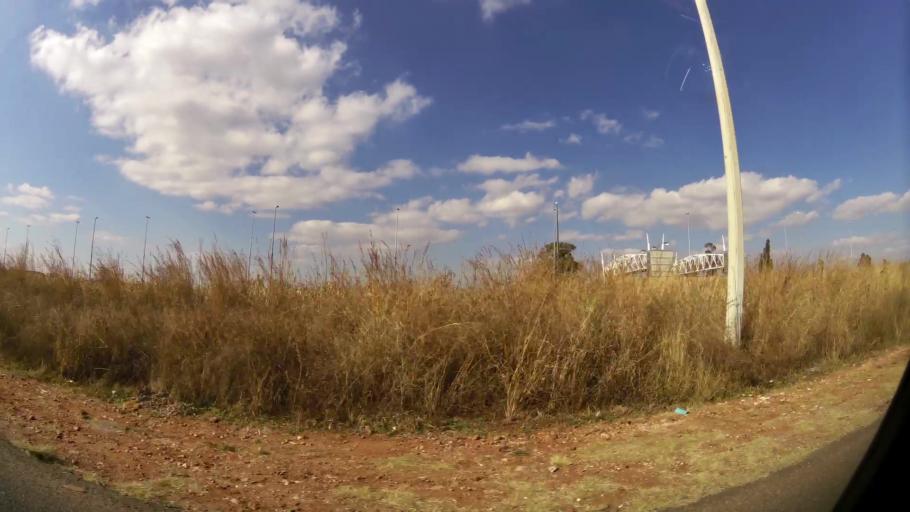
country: ZA
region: Gauteng
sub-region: Ekurhuleni Metropolitan Municipality
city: Tembisa
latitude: -25.9963
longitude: 28.2492
